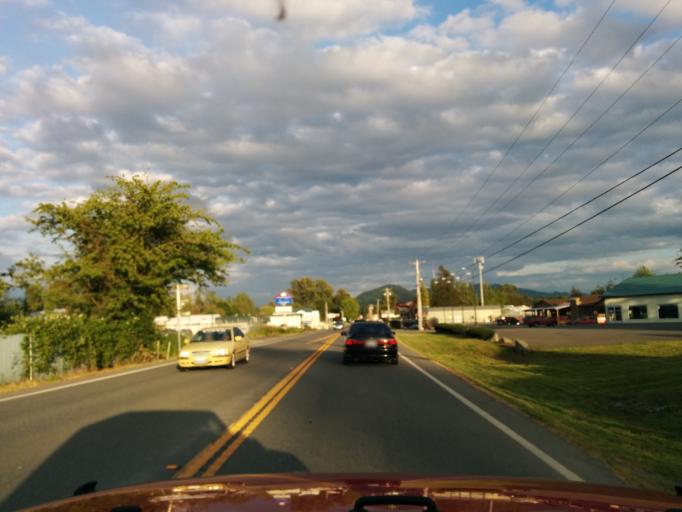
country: US
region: Washington
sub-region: Skagit County
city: Mount Vernon
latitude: 48.4273
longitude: -122.3612
